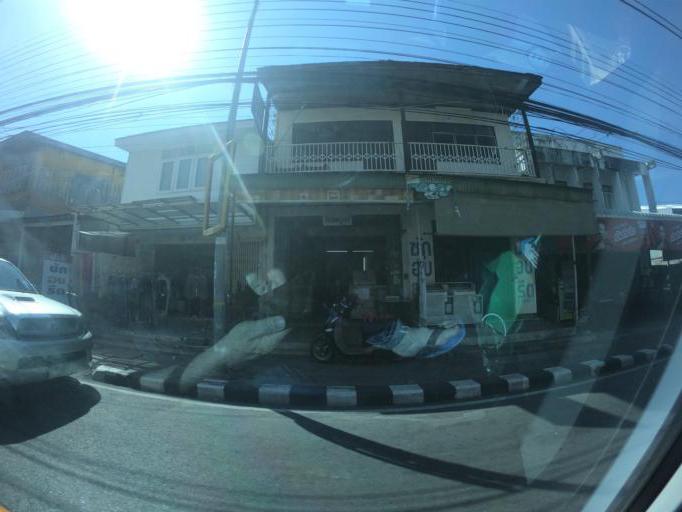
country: TH
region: Khon Kaen
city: Khon Kaen
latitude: 16.4196
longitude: 102.8345
